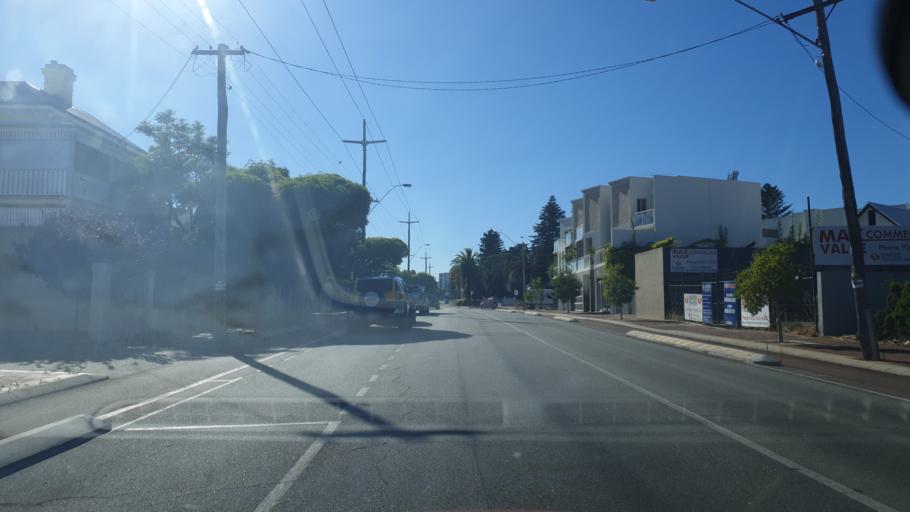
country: AU
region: Western Australia
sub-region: Vincent
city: Mount Lawley
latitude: -31.9432
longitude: 115.8685
